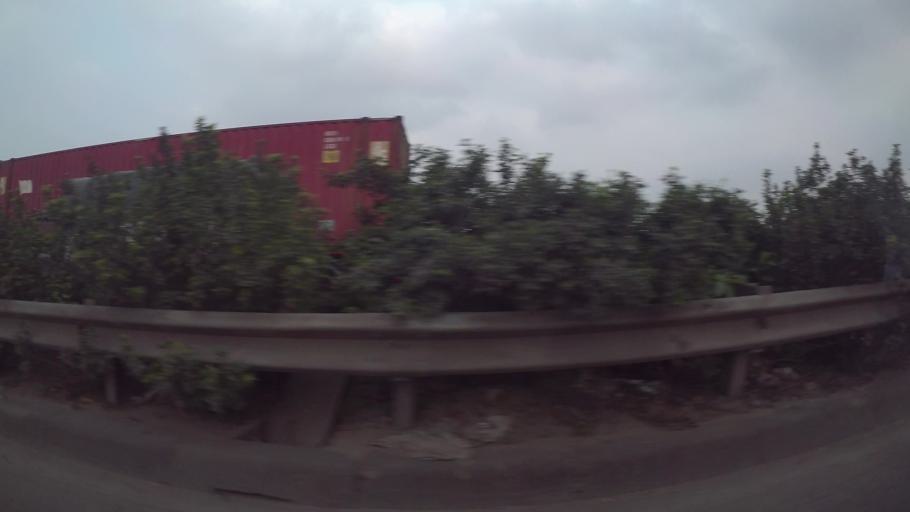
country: VN
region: Ha Noi
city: Trau Quy
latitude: 21.0142
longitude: 105.9193
